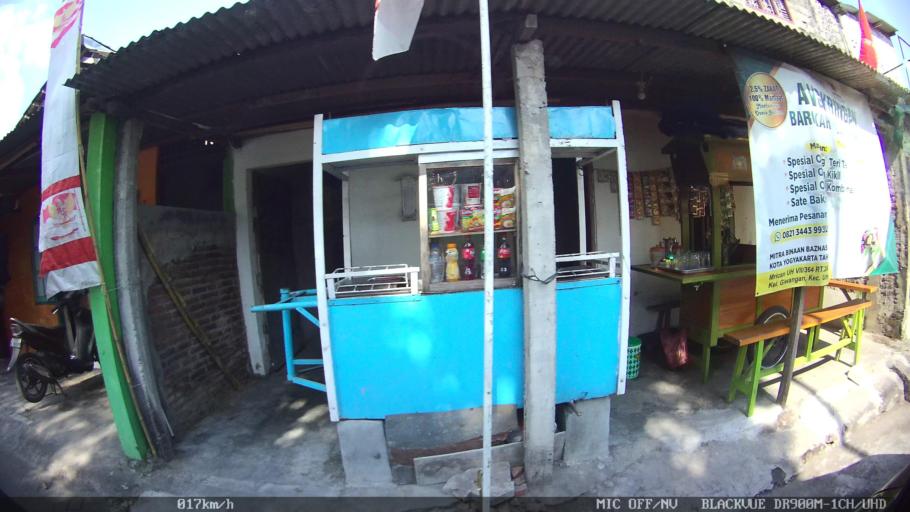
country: ID
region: Daerah Istimewa Yogyakarta
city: Sewon
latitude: -7.8328
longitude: 110.3933
